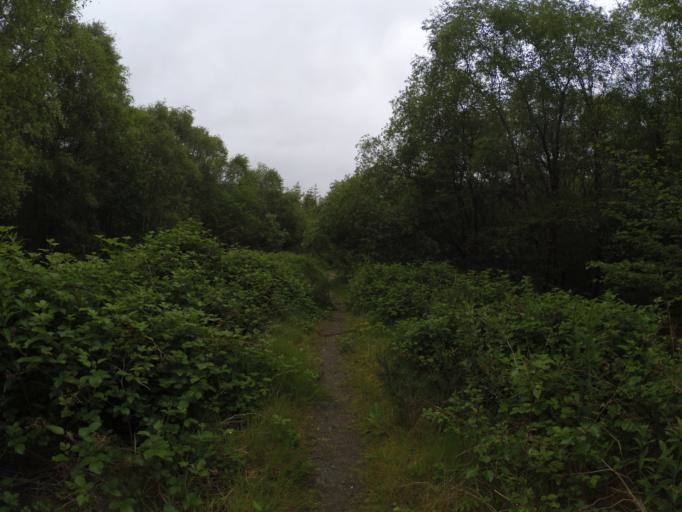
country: GB
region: Wales
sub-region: County of Ceredigion
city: Llangybi
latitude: 52.1685
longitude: -4.0617
